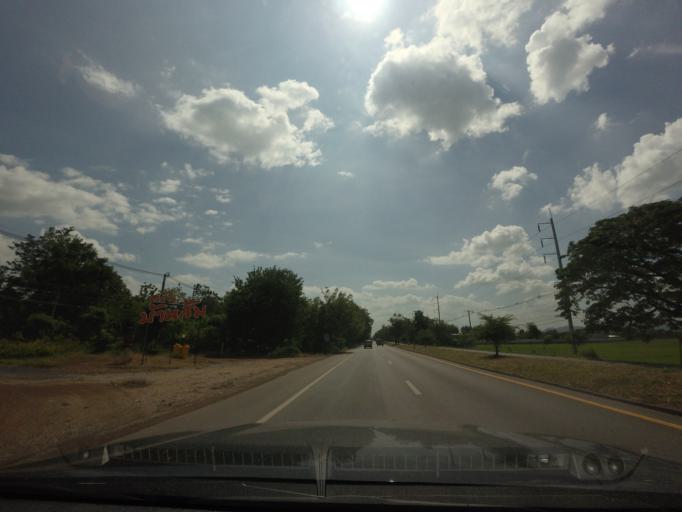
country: TH
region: Phetchabun
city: Nong Phai
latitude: 15.9500
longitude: 101.0372
